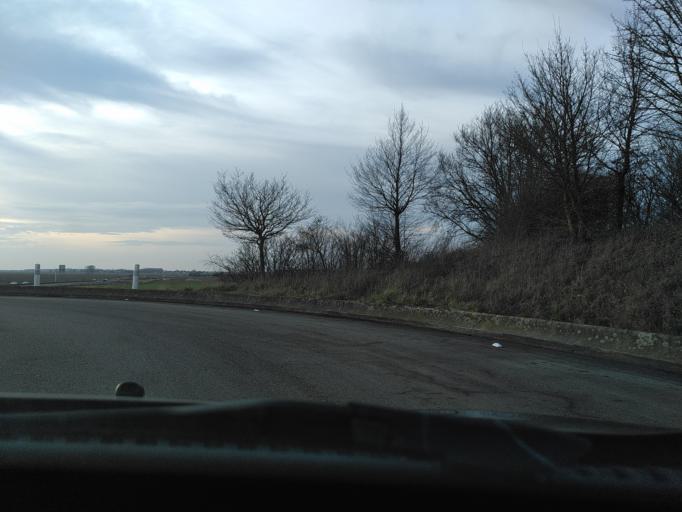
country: FR
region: Picardie
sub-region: Departement de la Somme
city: Villers-Bretonneux
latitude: 49.8547
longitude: 2.5191
